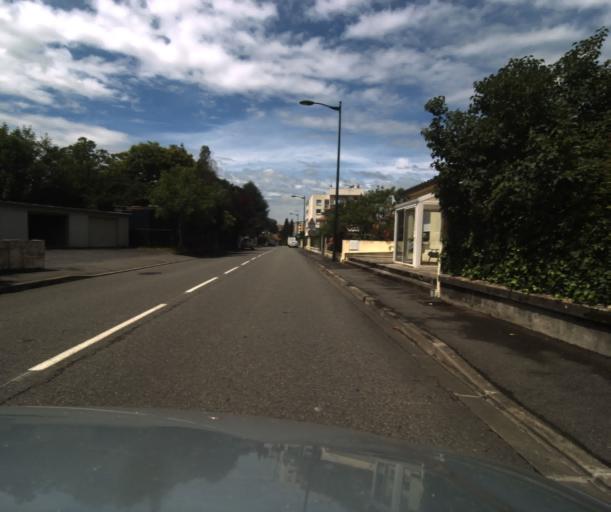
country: FR
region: Midi-Pyrenees
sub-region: Departement des Hautes-Pyrenees
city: Lourdes
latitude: 43.0853
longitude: -0.0480
